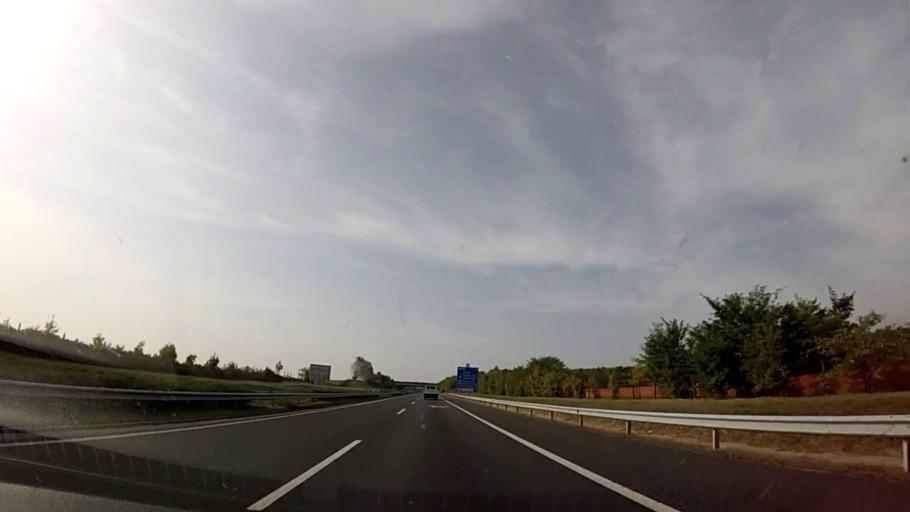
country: HU
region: Somogy
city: Kethely
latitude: 46.6755
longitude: 17.3567
